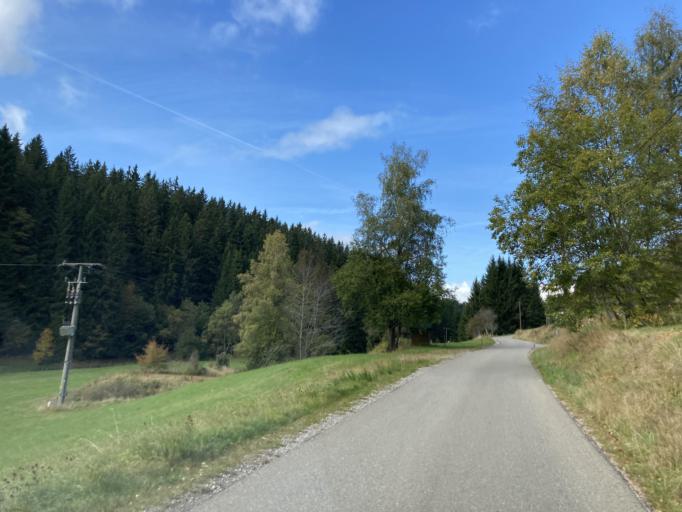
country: DE
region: Baden-Wuerttemberg
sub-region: Freiburg Region
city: Vohrenbach
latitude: 48.0664
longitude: 8.2832
